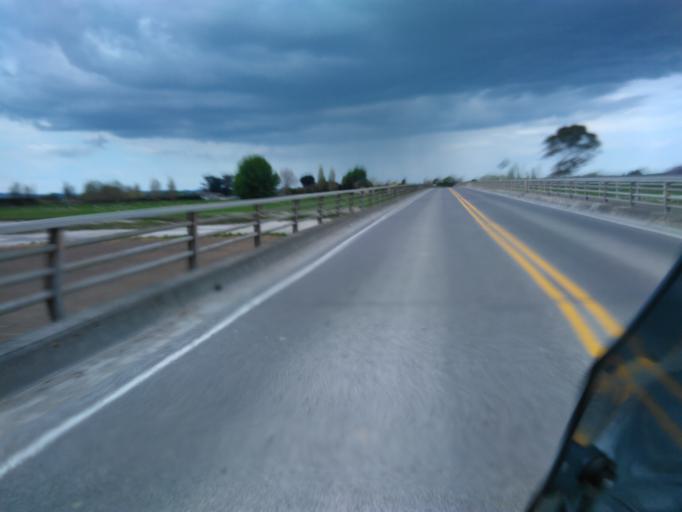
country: NZ
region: Gisborne
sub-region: Gisborne District
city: Gisborne
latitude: -38.6530
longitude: 177.9166
